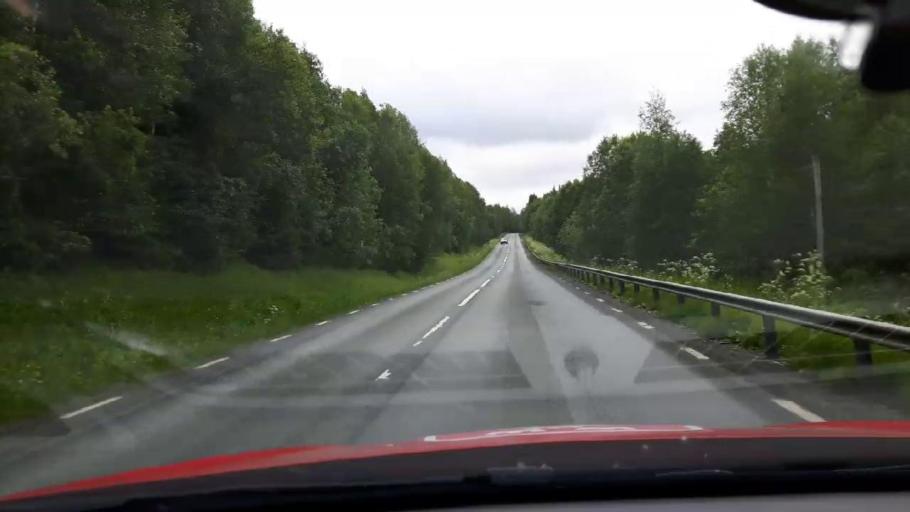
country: SE
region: Jaemtland
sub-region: Are Kommun
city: Are
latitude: 63.3915
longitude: 12.7759
